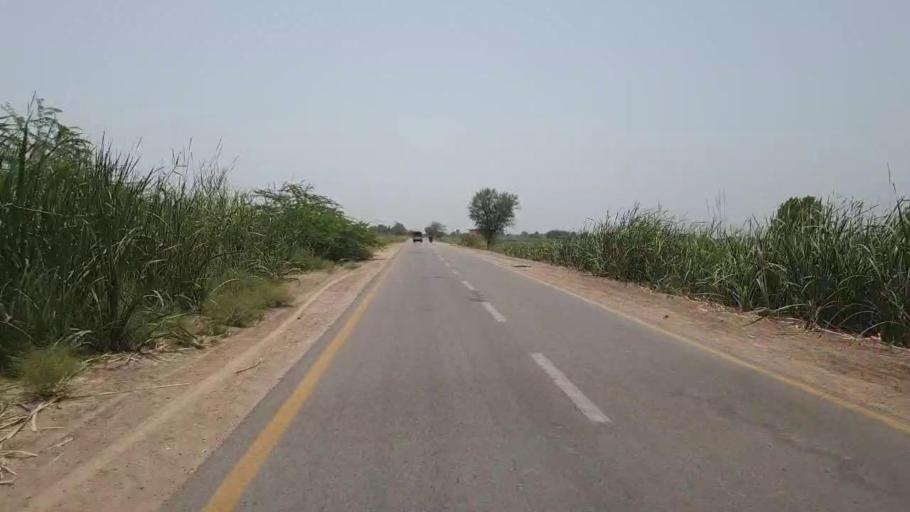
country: PK
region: Sindh
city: Moro
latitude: 26.6022
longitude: 68.0631
